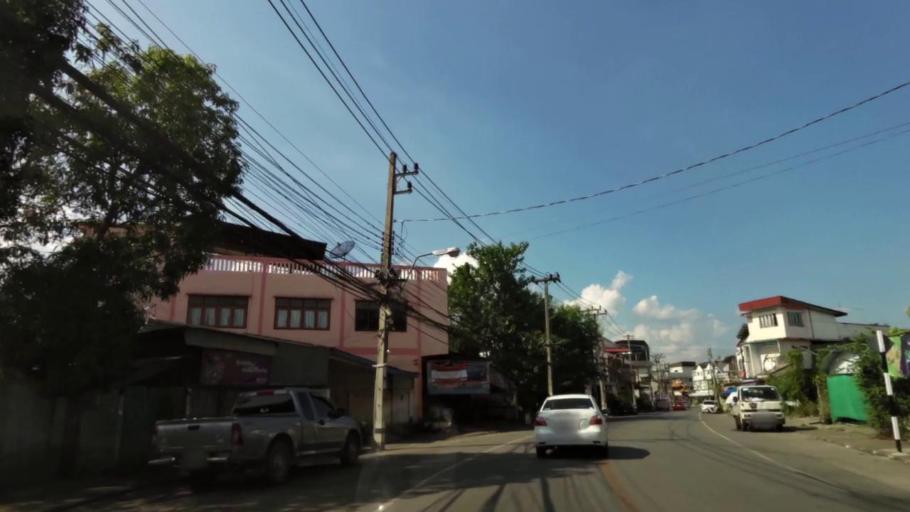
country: TH
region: Phrae
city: Phrae
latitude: 18.1391
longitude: 100.1435
